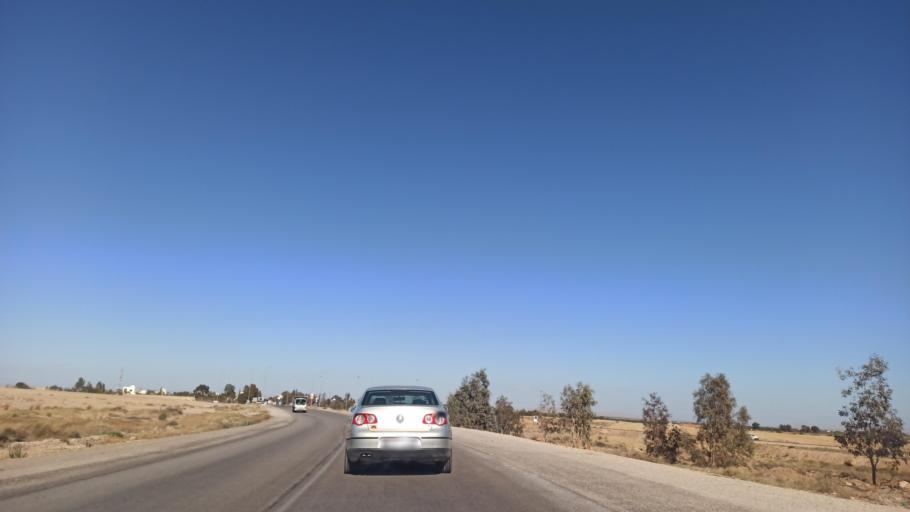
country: TN
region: Sidi Bu Zayd
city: Jilma
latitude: 35.1368
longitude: 9.3604
